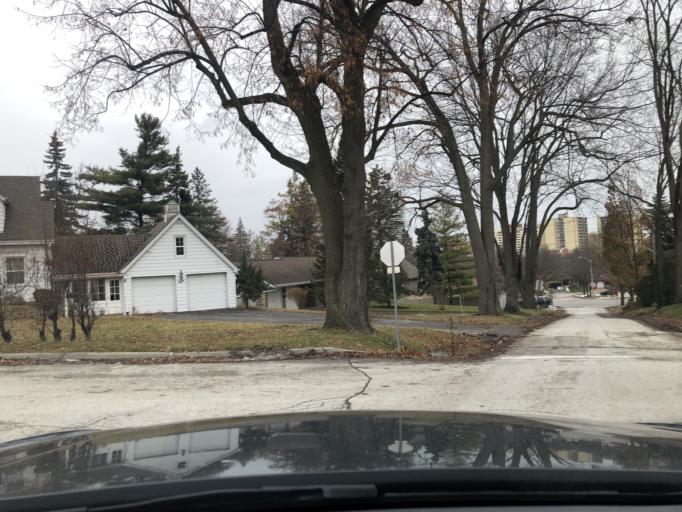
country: CA
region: Ontario
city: Etobicoke
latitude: 43.6963
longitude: -79.5230
